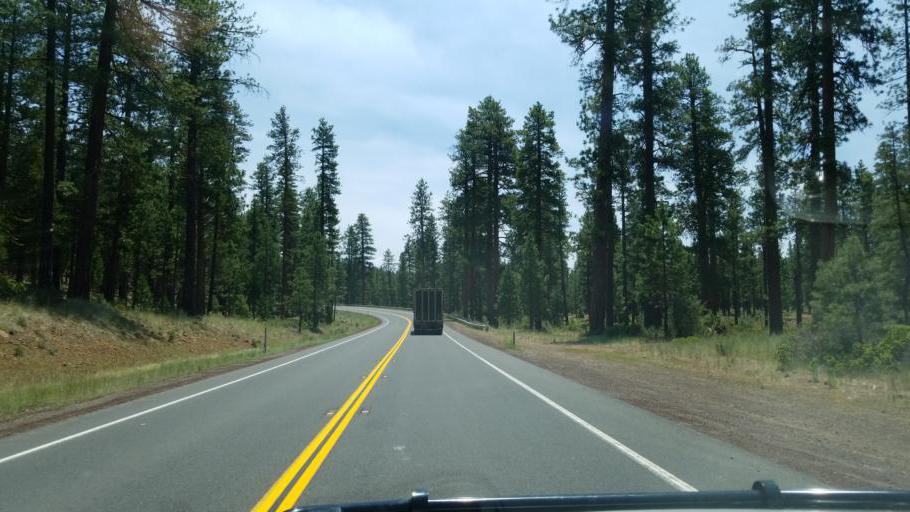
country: US
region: California
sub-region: Shasta County
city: Burney
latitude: 40.6670
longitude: -121.3581
